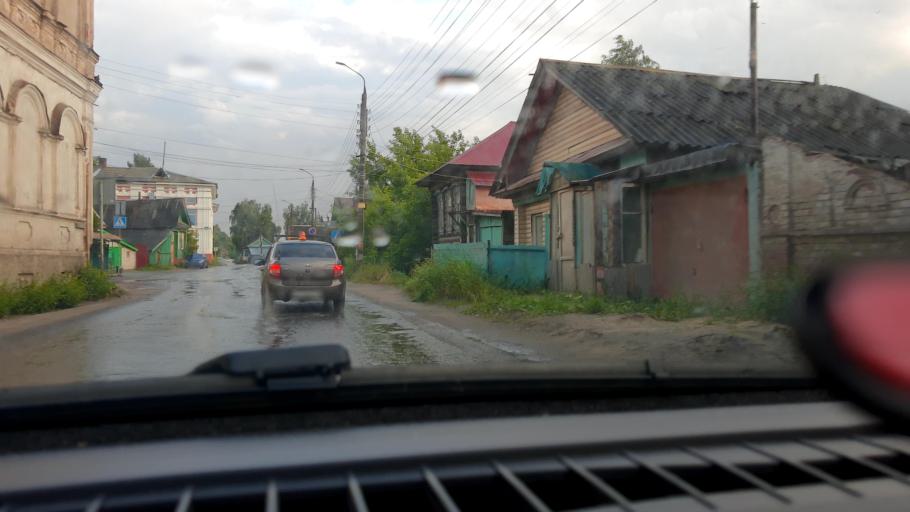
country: RU
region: Nizjnij Novgorod
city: Gorodets
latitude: 56.6559
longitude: 43.4642
